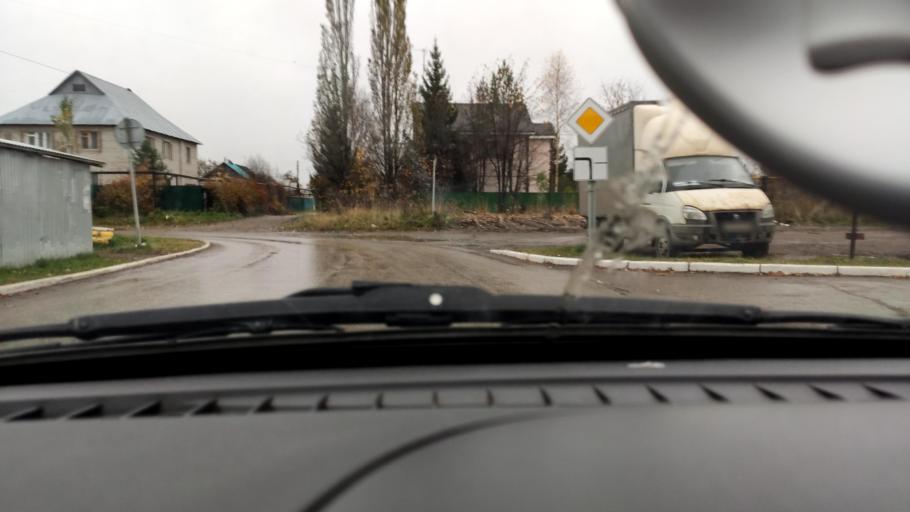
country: RU
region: Perm
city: Kondratovo
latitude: 57.9747
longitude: 56.1026
